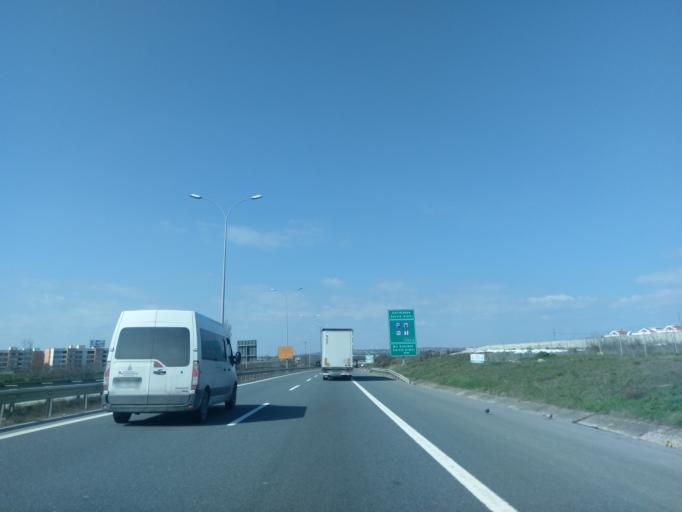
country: TR
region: Istanbul
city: Selimpasa
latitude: 41.0761
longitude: 28.3758
